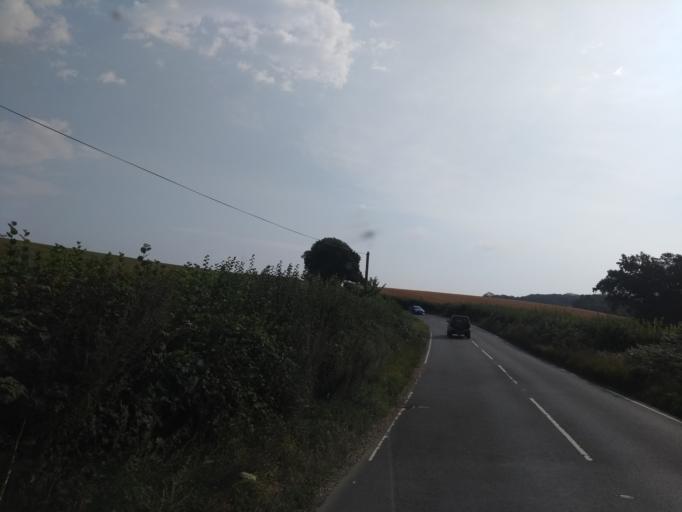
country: GB
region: England
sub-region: Devon
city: Axminster
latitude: 50.7591
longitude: -3.0198
